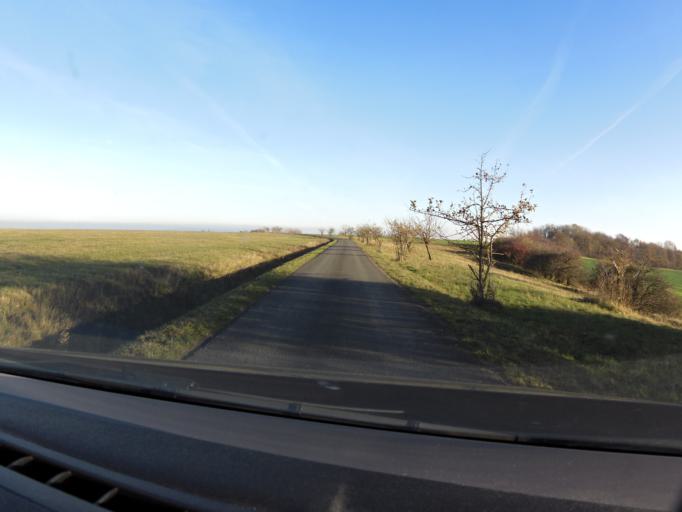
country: DE
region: Thuringia
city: Weberstedt
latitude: 51.0652
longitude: 10.4741
